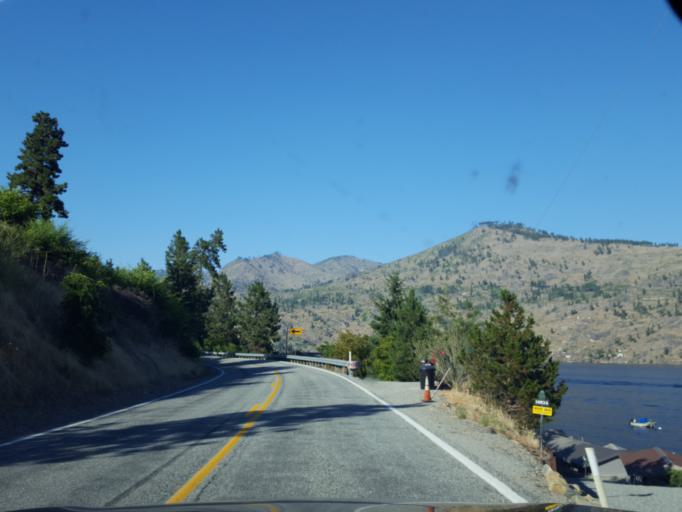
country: US
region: Washington
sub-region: Chelan County
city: Granite Falls
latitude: 47.9464
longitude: -120.2095
